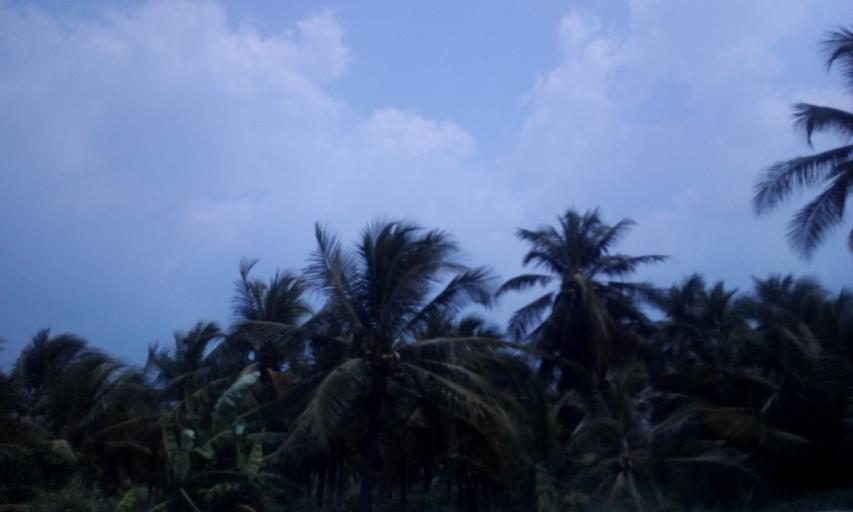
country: TH
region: Chon Buri
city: Ban Bueng
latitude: 13.3420
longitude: 101.1919
